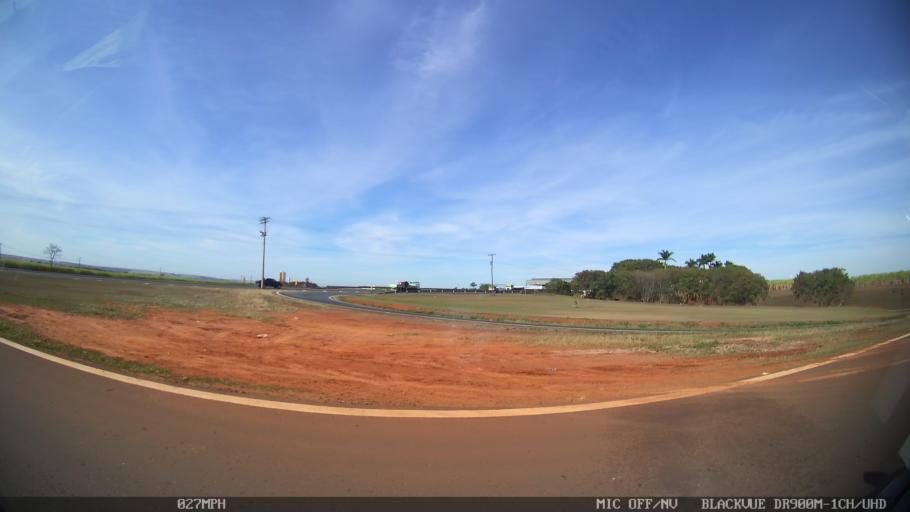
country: BR
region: Sao Paulo
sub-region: Piracicaba
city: Piracicaba
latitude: -22.7806
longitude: -47.6528
